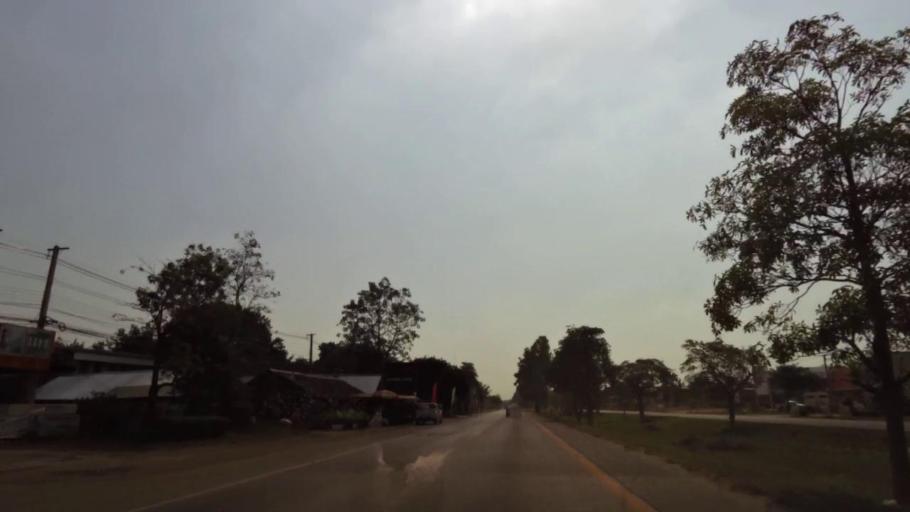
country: TH
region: Phichit
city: Wachira Barami
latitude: 16.5026
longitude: 100.1437
